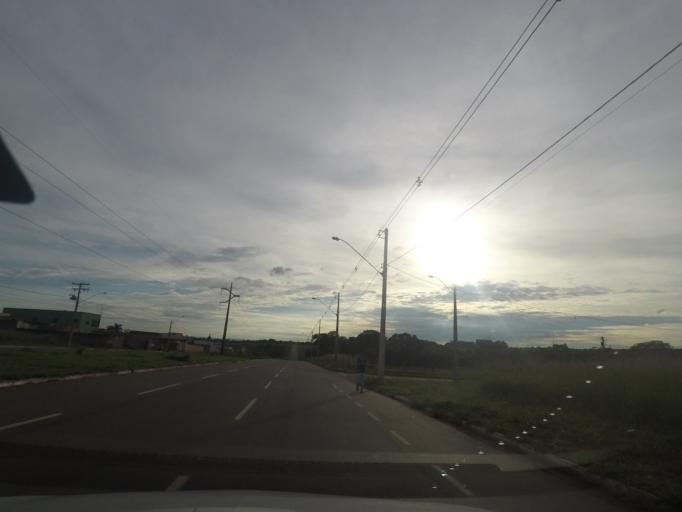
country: BR
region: Goias
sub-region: Trindade
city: Trindade
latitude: -16.7193
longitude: -49.3935
